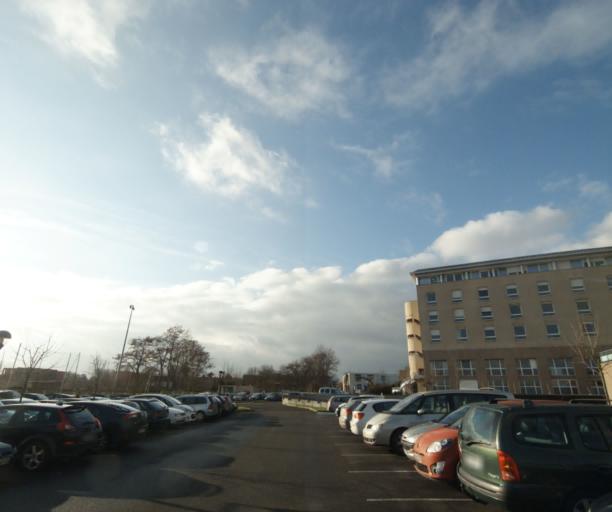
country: FR
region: Pays de la Loire
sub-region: Departement de la Sarthe
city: La Chapelle-Saint-Aubin
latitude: 48.0186
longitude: 0.1642
